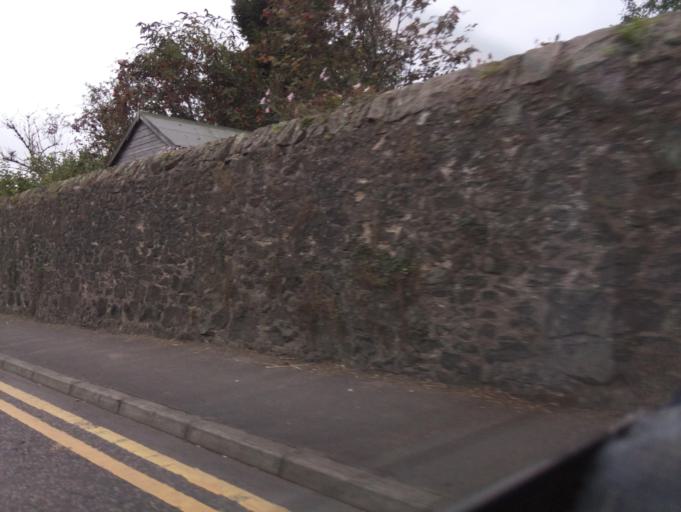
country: GB
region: Scotland
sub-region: Fife
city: Leslie
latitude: 56.2021
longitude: -3.2180
